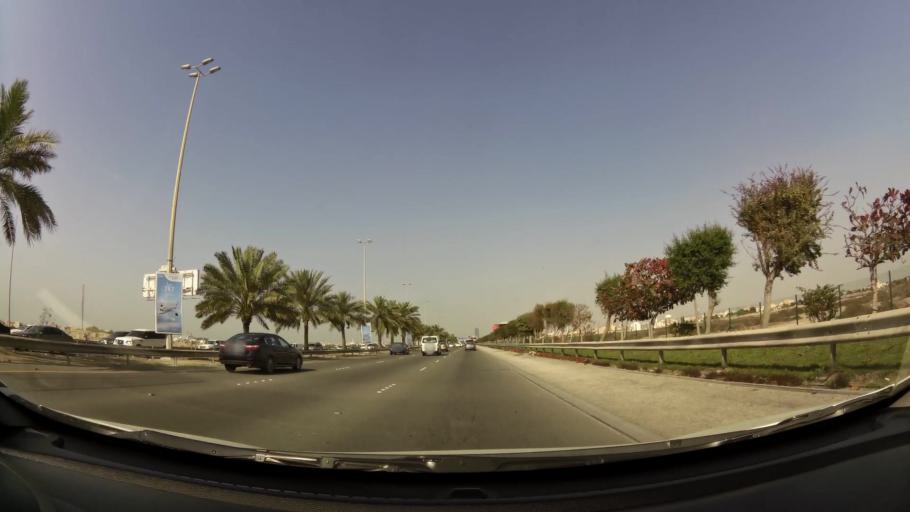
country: BH
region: Manama
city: Jidd Hafs
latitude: 26.2010
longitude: 50.5114
